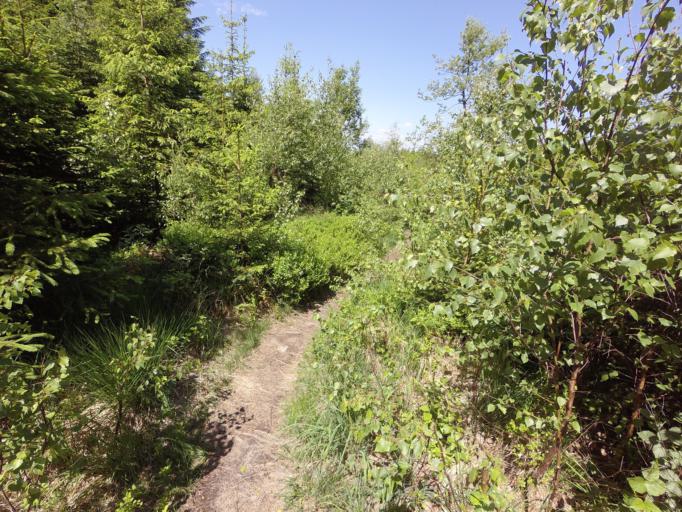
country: BE
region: Wallonia
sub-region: Province de Liege
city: Jalhay
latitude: 50.5163
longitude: 6.0069
